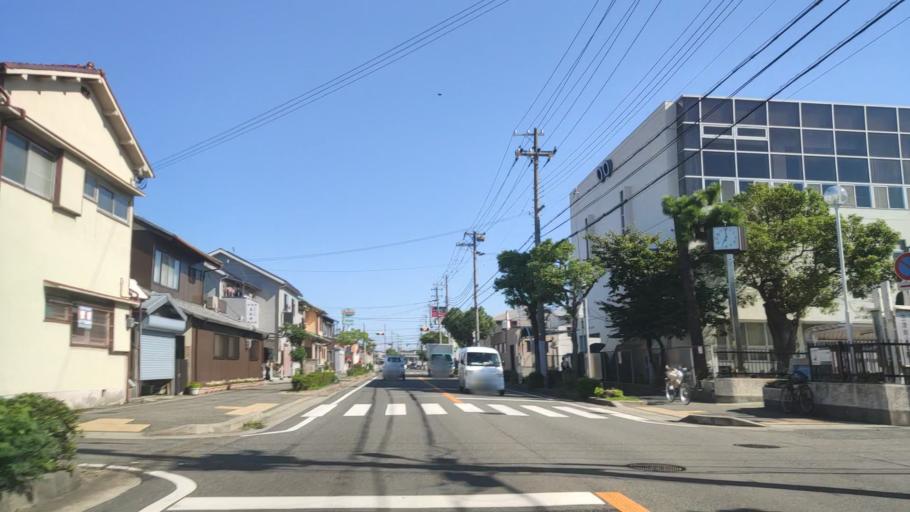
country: JP
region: Hyogo
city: Akashi
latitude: 34.6600
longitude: 134.9903
